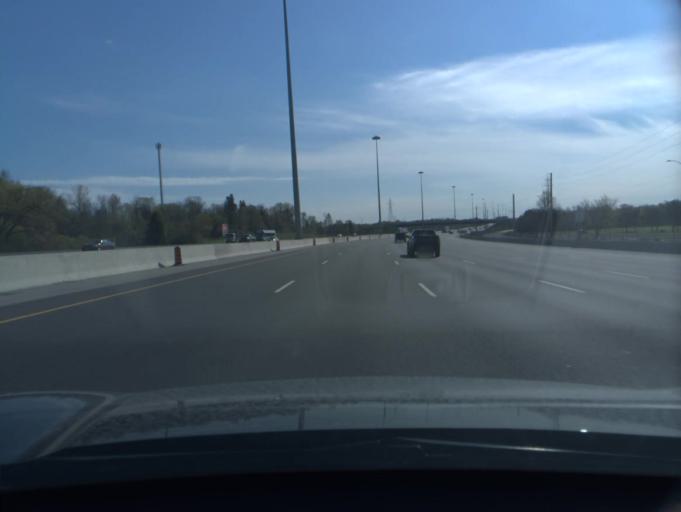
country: CA
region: Ontario
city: North Perth
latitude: 43.8253
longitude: -81.0000
